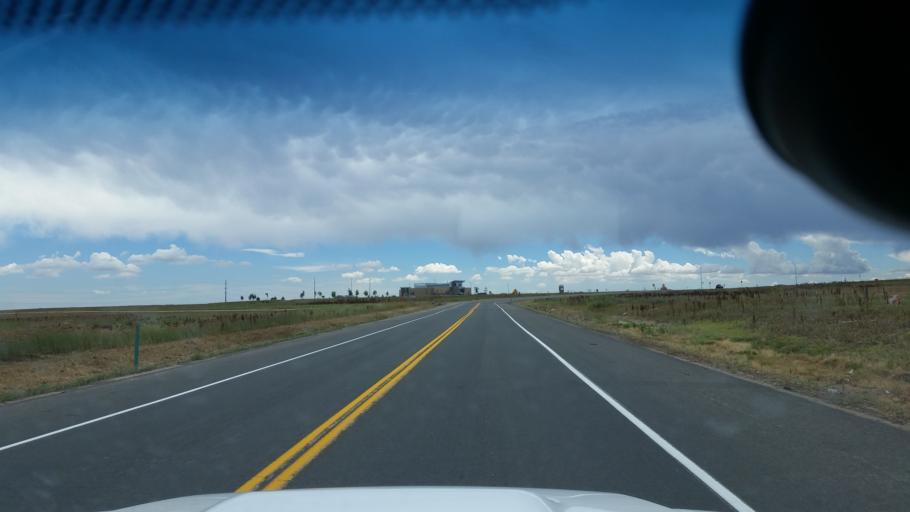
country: US
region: Colorado
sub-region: Weld County
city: Dacono
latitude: 40.0473
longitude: -104.9787
